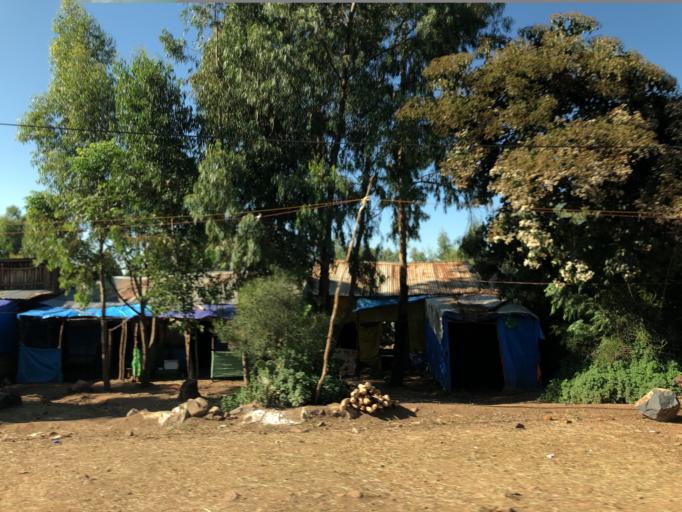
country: ET
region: Amhara
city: Gondar
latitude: 12.4747
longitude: 37.4831
